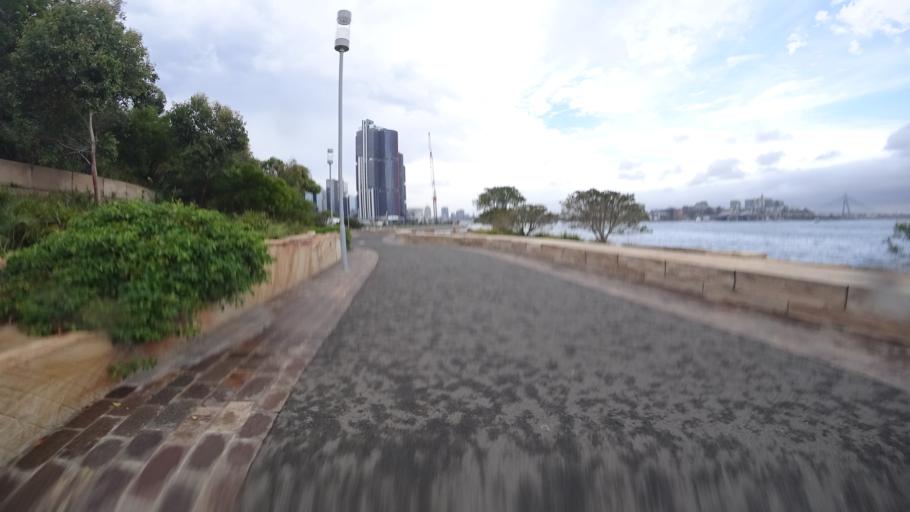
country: AU
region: New South Wales
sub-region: Leichhardt
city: Balmain East
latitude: -33.8579
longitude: 151.2003
